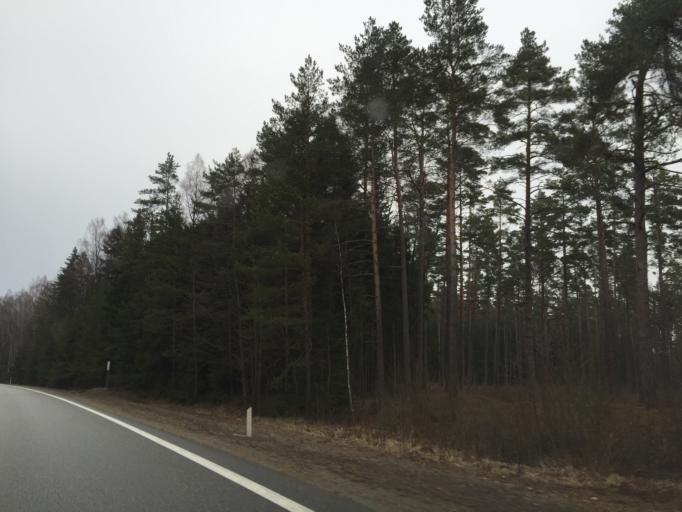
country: LV
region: Salacgrivas
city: Salacgriva
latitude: 57.5759
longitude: 24.4337
